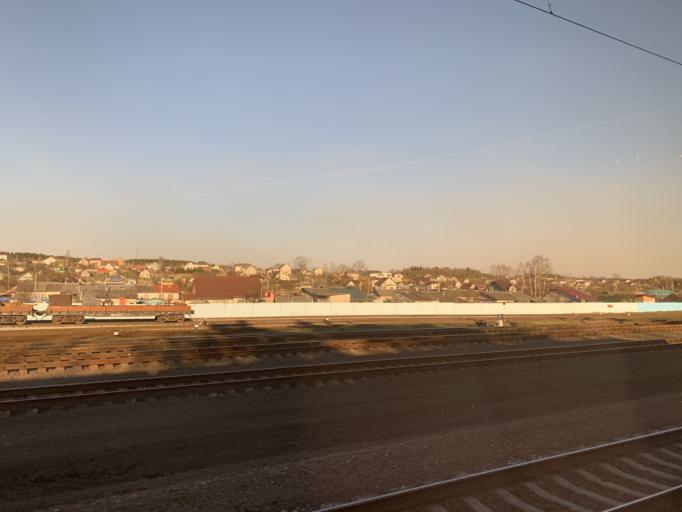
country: BY
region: Minsk
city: Pyatryshki
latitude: 54.0670
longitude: 27.2141
